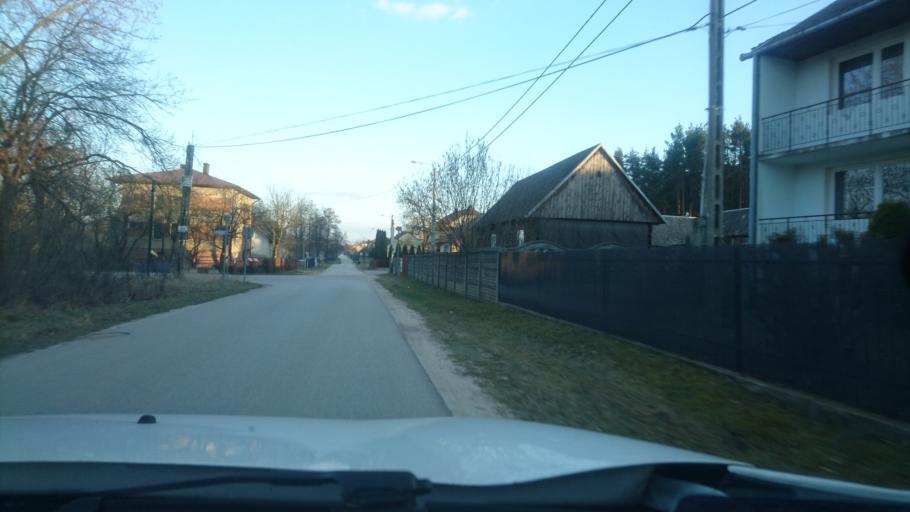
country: PL
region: Swietokrzyskie
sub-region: Powiat kielecki
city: Pierzchnica
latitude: 50.7773
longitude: 20.7074
